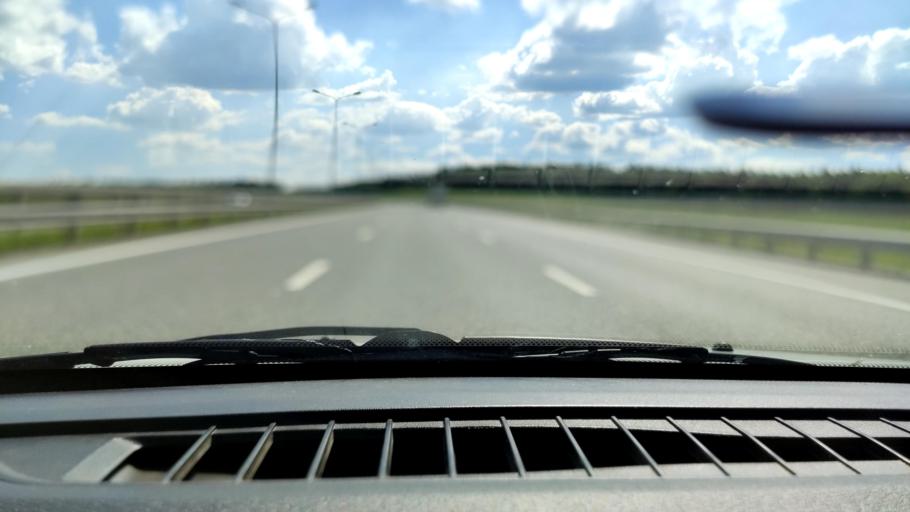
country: RU
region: Perm
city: Zvezdnyy
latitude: 57.7701
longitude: 56.3358
